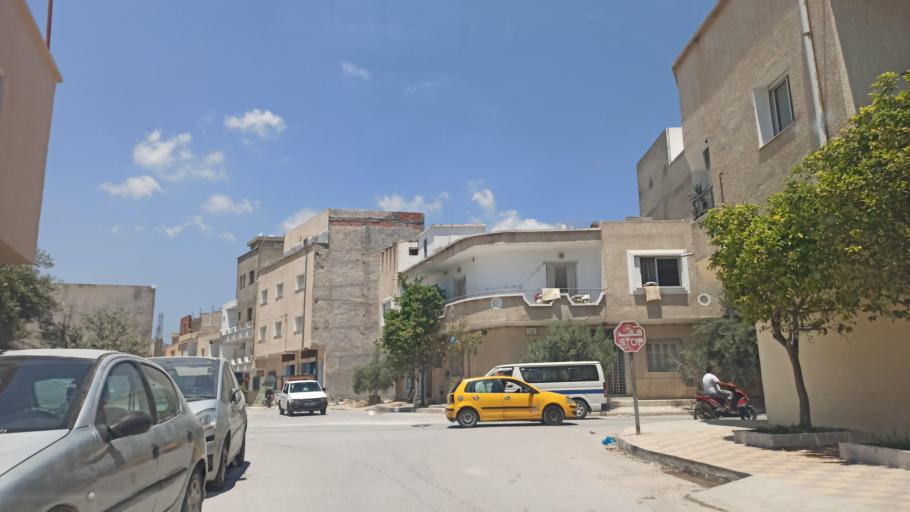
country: TN
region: Nabul
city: Dar Chabanne
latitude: 36.4685
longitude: 10.7433
